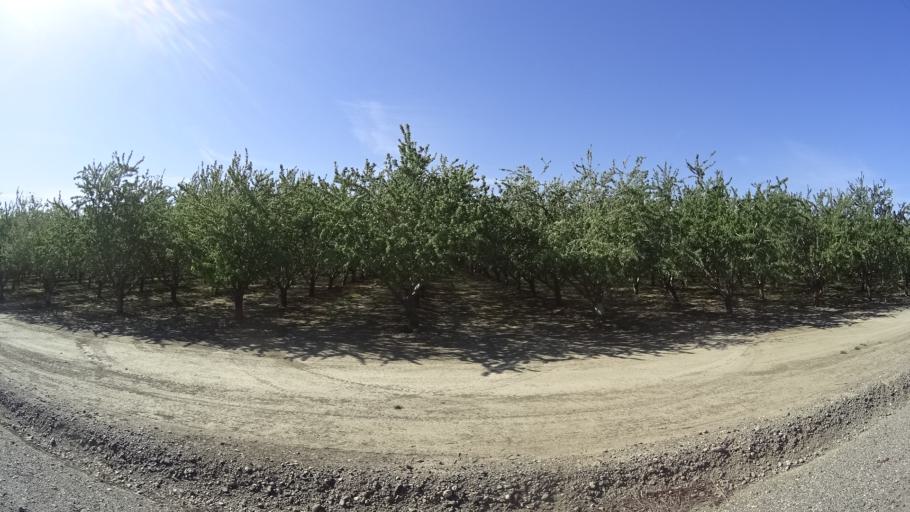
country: US
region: California
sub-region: Glenn County
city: Willows
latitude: 39.6113
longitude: -122.1742
